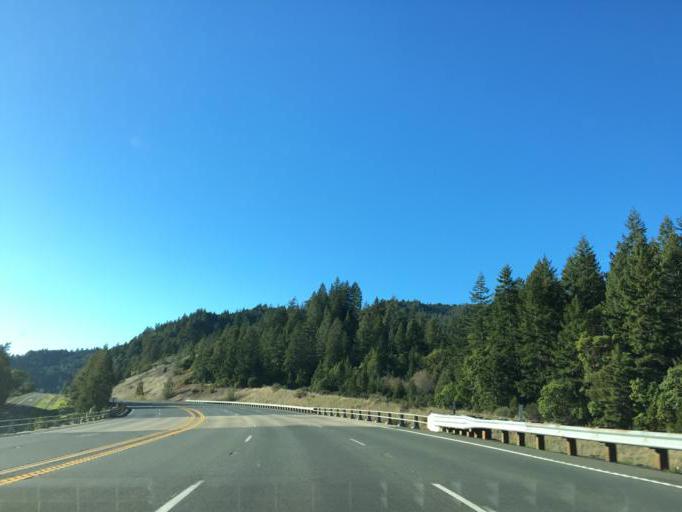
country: US
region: California
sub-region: Mendocino County
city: Laytonville
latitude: 39.8346
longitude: -123.6310
